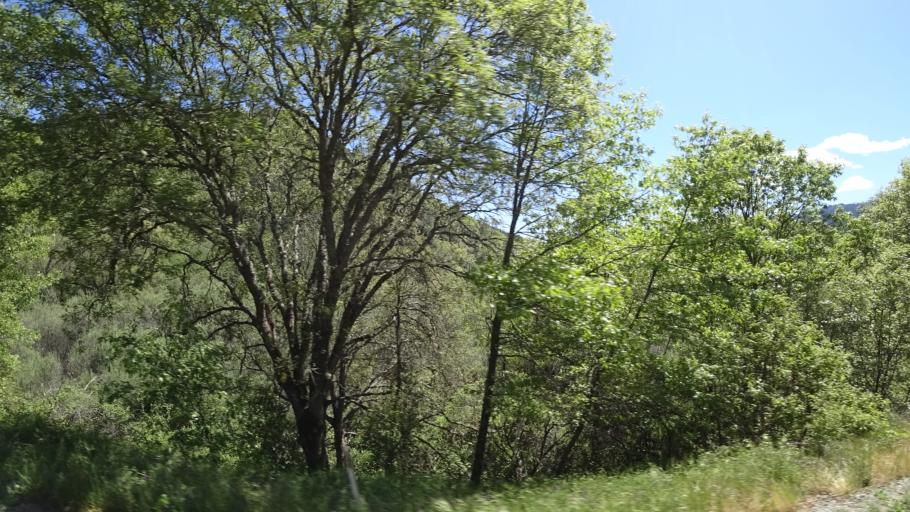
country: US
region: California
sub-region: Trinity County
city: Weaverville
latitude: 40.7296
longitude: -123.0360
